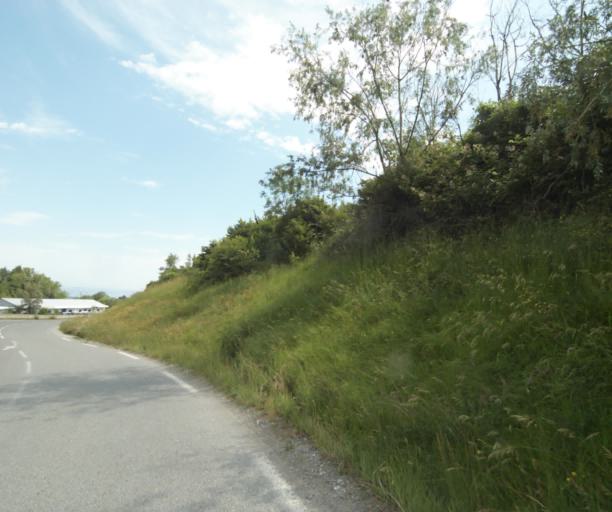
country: FR
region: Rhone-Alpes
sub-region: Departement de la Haute-Savoie
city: Thonon-les-Bains
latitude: 46.3627
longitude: 6.4959
